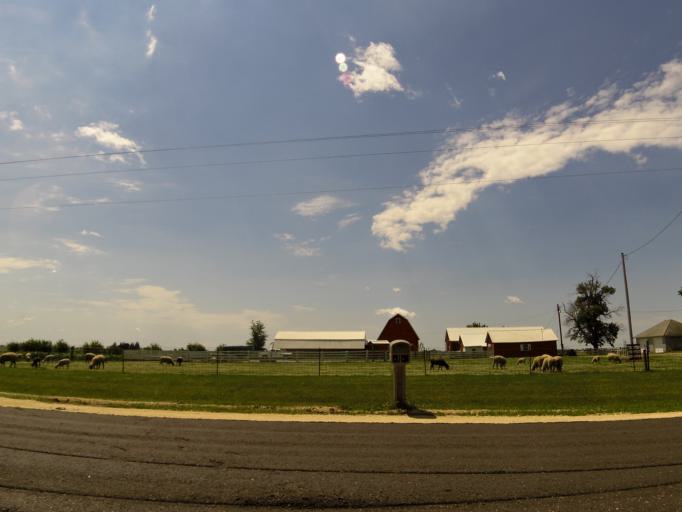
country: US
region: Iowa
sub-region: Bremer County
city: Denver
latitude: 42.7150
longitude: -92.3107
